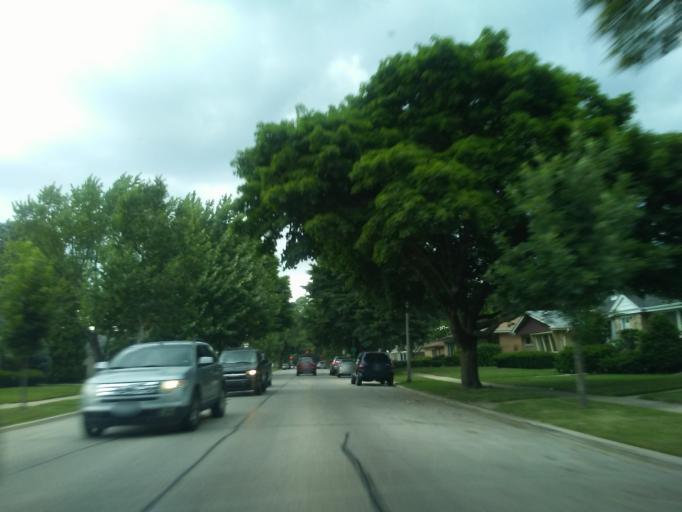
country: US
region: Illinois
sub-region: Cook County
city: Skokie
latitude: 42.0236
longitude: -87.7379
